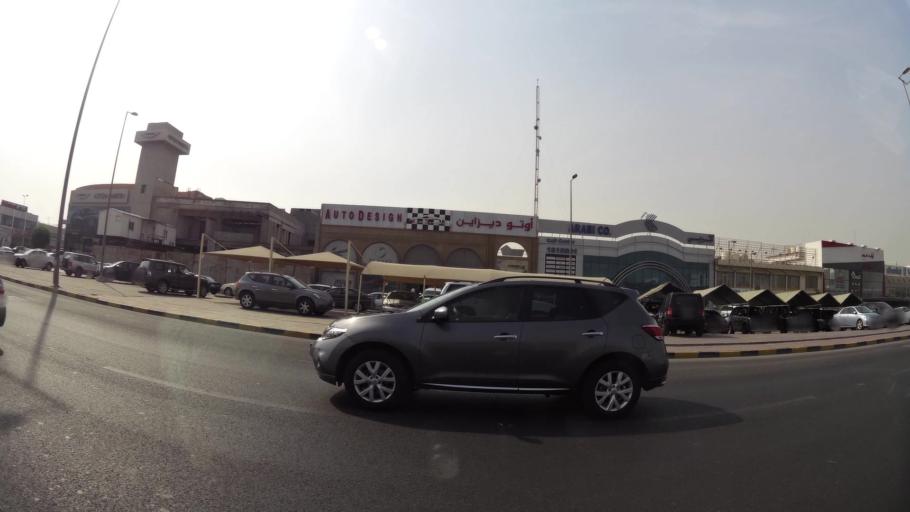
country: KW
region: Al Asimah
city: Ar Rabiyah
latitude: 29.3095
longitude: 47.9433
